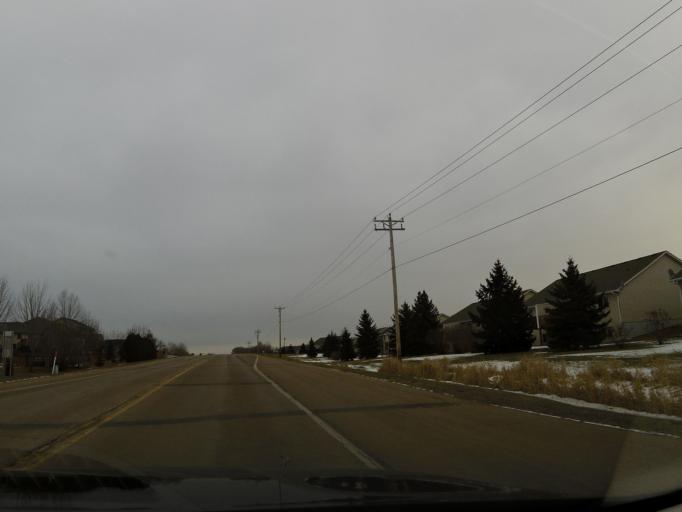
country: US
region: Minnesota
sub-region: Carver County
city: Waconia
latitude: 44.8551
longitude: -93.8170
